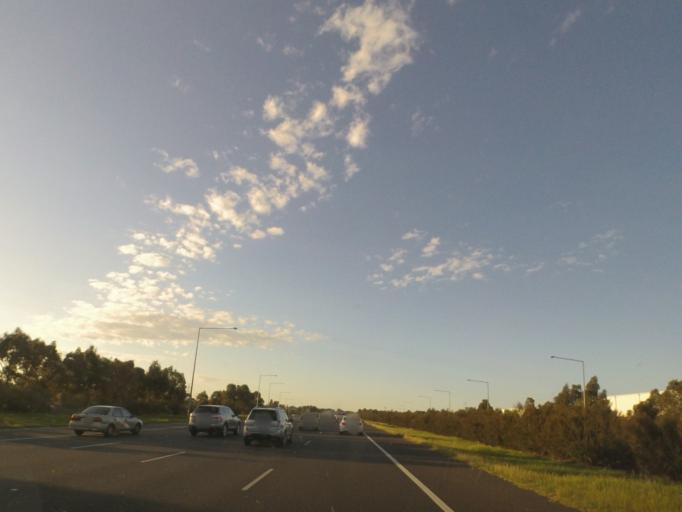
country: AU
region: Victoria
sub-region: Monash
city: Mulgrave
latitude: -37.9080
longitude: 145.2159
